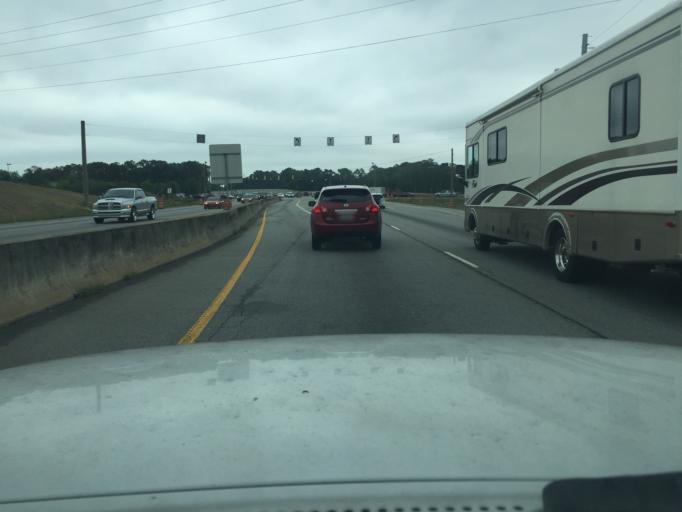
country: US
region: Georgia
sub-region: Chatham County
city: Georgetown
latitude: 31.9866
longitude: -81.2192
